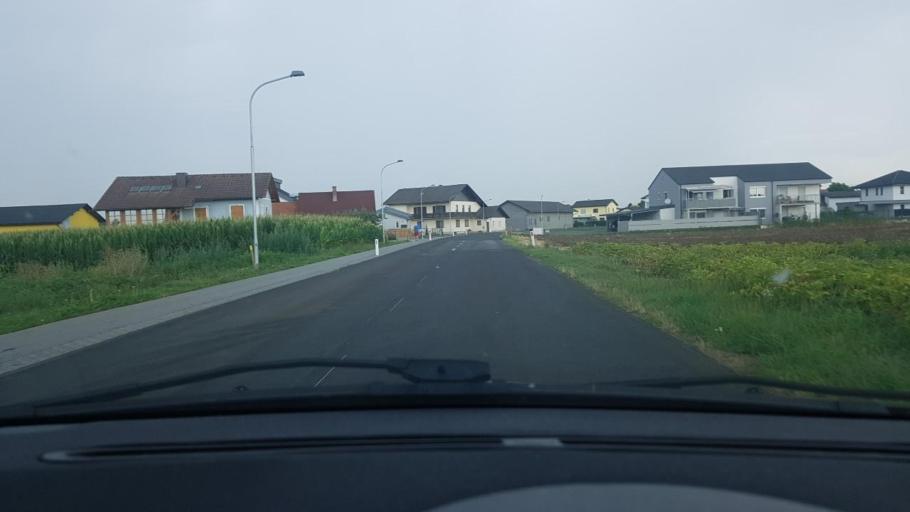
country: AT
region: Styria
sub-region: Politischer Bezirk Graz-Umgebung
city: Wundschuh
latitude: 46.9328
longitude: 15.4477
